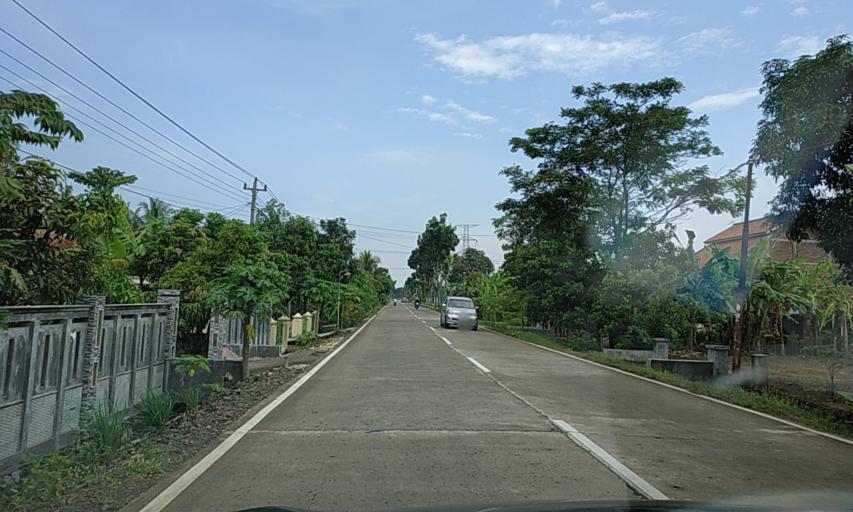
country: ID
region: Central Java
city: Tambangan
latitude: -7.4832
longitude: 108.8324
